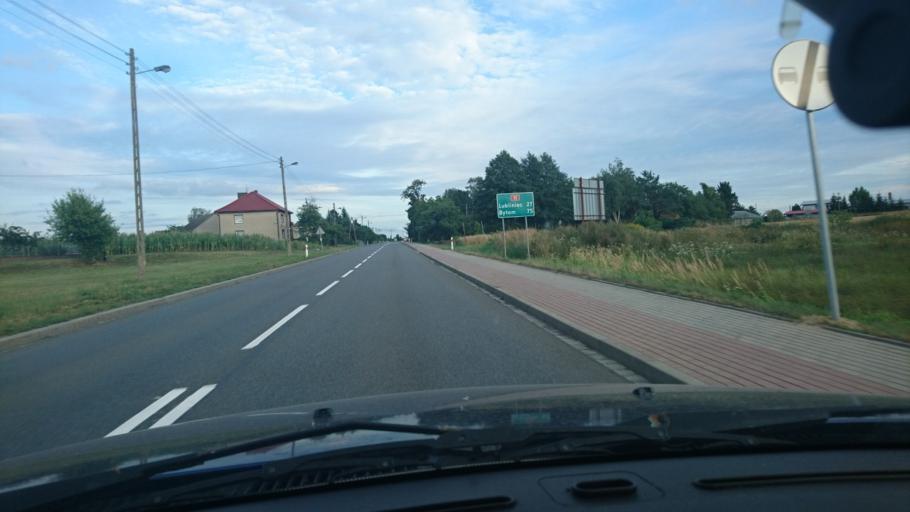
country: PL
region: Opole Voivodeship
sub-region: Powiat oleski
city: Olesno
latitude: 50.8714
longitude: 18.4309
